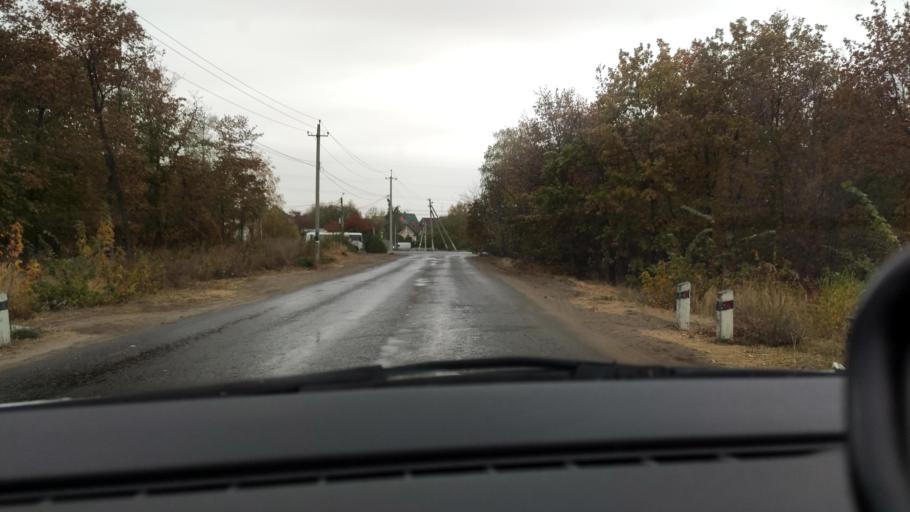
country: RU
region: Voronezj
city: Pridonskoy
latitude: 51.6412
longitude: 39.0937
